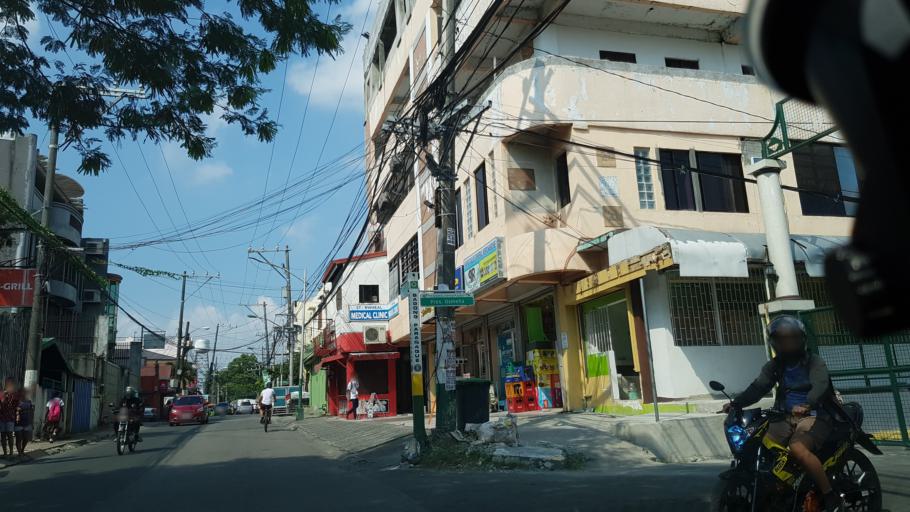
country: PH
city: Sambayanihan People's Village
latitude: 14.4747
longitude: 121.0249
